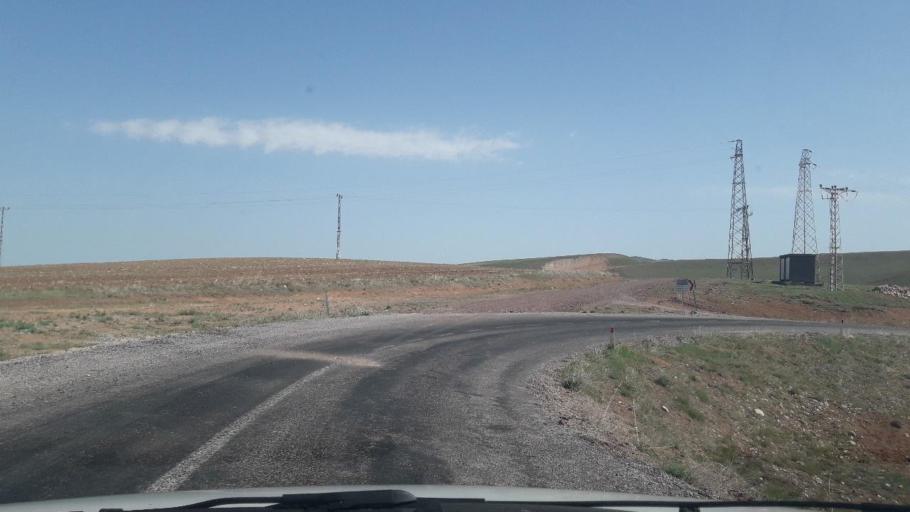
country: TR
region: Sivas
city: Alacahan
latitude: 39.0752
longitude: 37.5462
